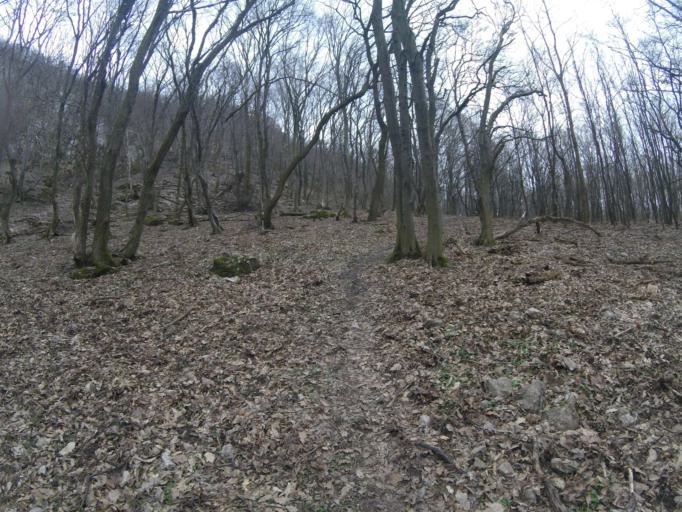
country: HU
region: Komarom-Esztergom
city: Piliscsev
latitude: 47.6875
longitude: 18.8413
